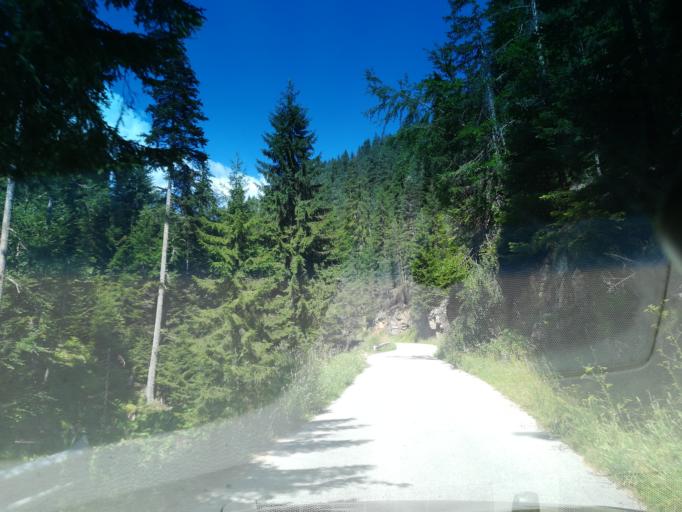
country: BG
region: Smolyan
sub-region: Obshtina Smolyan
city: Smolyan
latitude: 41.6598
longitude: 24.8121
